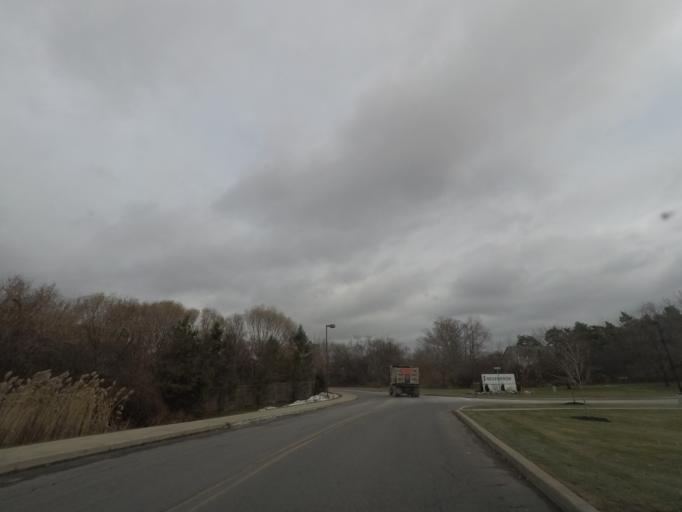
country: US
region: New York
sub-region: Rensselaer County
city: Hampton Manor
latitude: 42.6277
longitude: -73.7296
